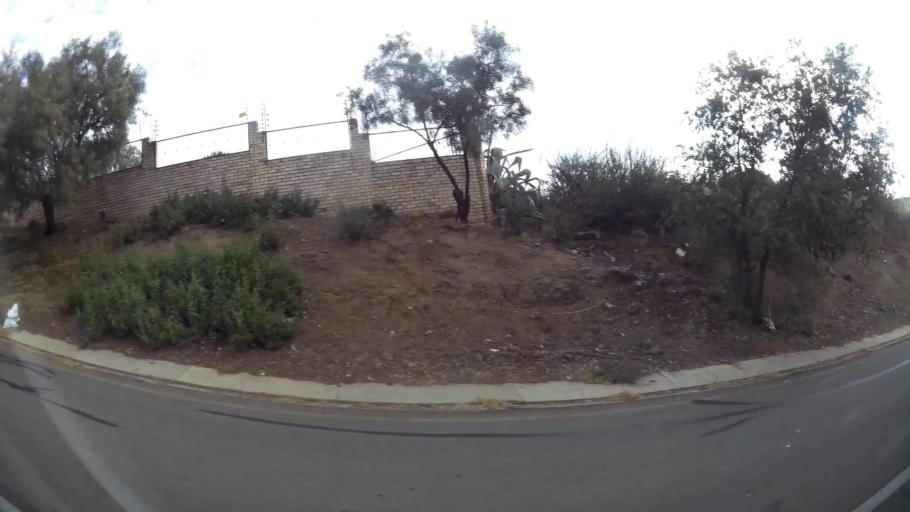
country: ZA
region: Orange Free State
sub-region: Mangaung Metropolitan Municipality
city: Bloemfontein
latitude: -29.0748
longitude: 26.2083
